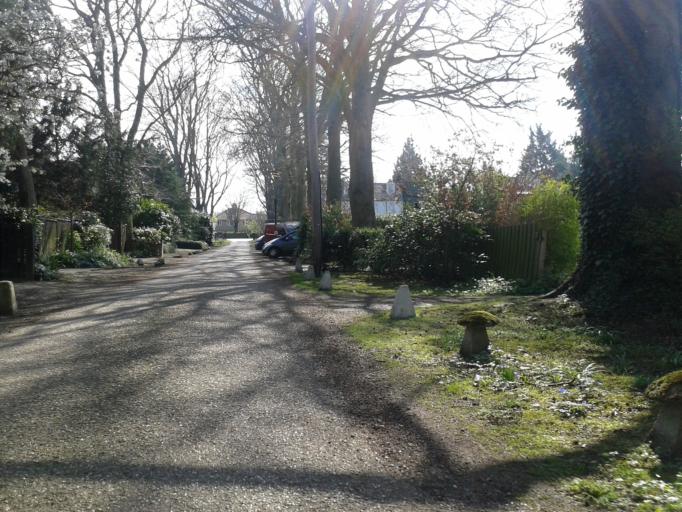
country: GB
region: England
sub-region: Cambridgeshire
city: Sawston
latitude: 52.1547
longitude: 0.1465
